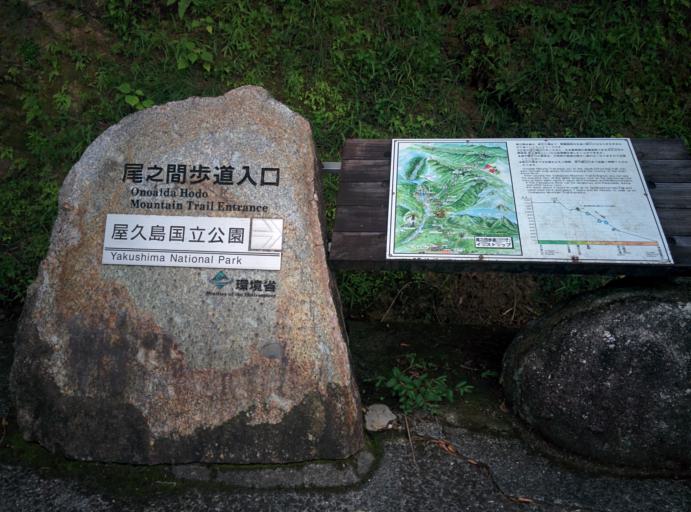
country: JP
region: Kagoshima
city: Nishinoomote
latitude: 30.2405
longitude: 130.5488
